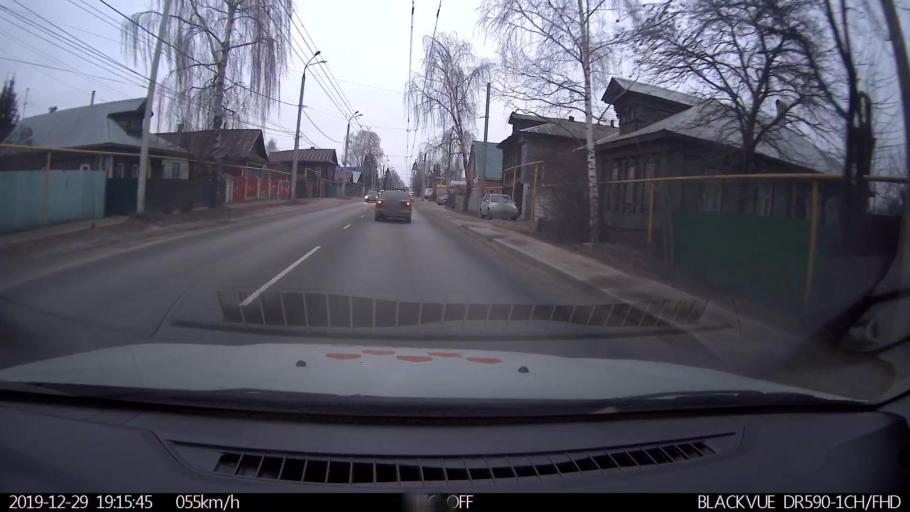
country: RU
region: Nizjnij Novgorod
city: Neklyudovo
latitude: 56.3754
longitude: 43.8349
